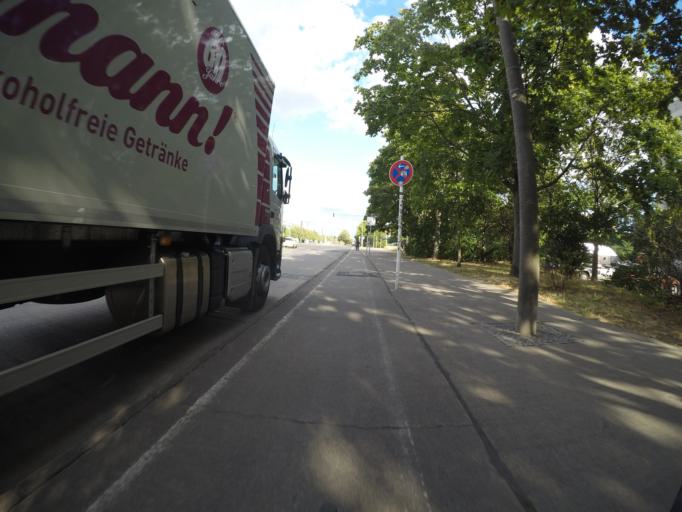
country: DE
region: Berlin
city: Hellersdorf
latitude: 52.5332
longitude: 13.6086
